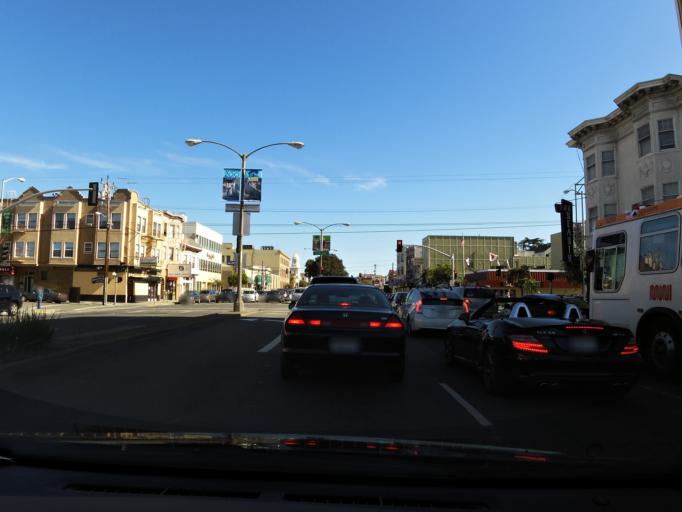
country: US
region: California
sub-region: San Francisco County
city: San Francisco
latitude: 37.7805
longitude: -122.4697
